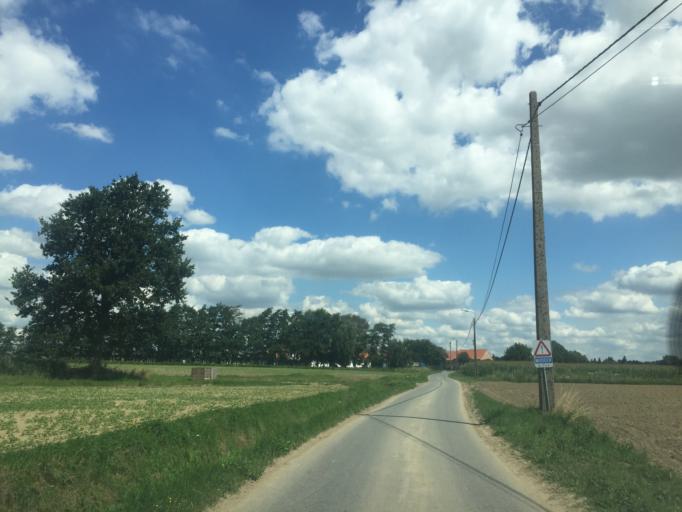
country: BE
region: Flanders
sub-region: Provincie West-Vlaanderen
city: Staden
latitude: 50.9641
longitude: 3.0508
